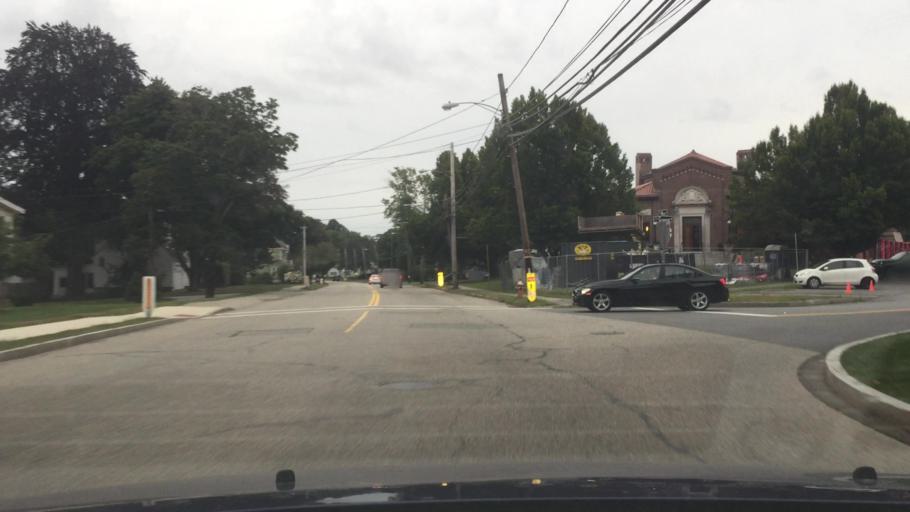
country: US
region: Massachusetts
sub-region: Essex County
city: North Andover
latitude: 42.6970
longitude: -71.1268
